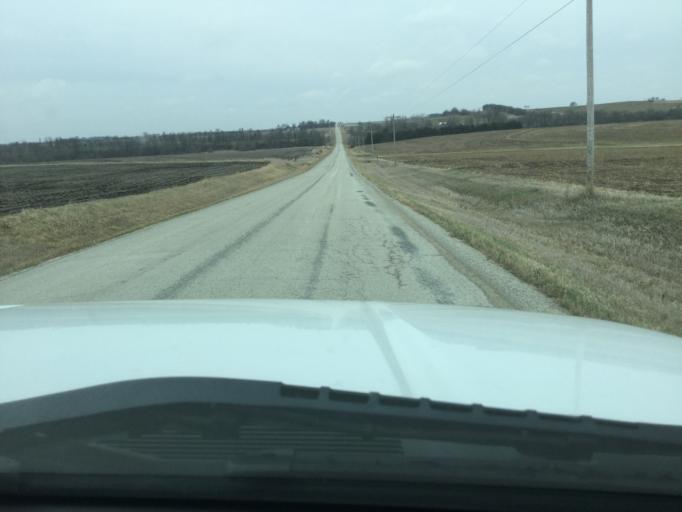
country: US
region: Kansas
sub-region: Nemaha County
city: Sabetha
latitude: 39.8971
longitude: -95.7138
